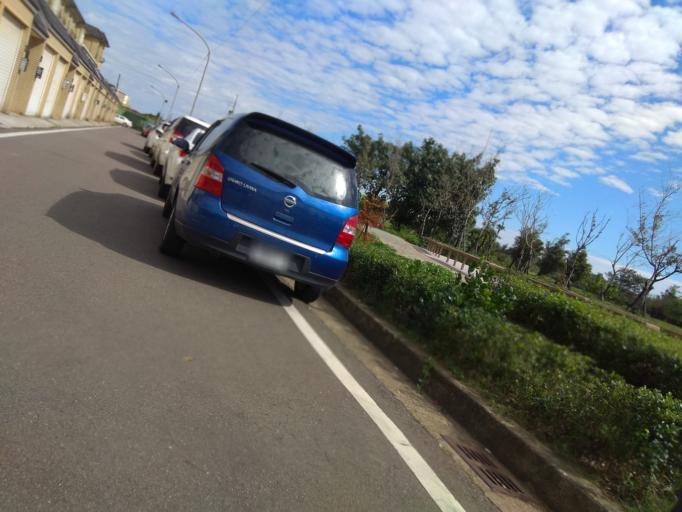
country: TW
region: Taiwan
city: Taoyuan City
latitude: 25.0487
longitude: 121.1209
